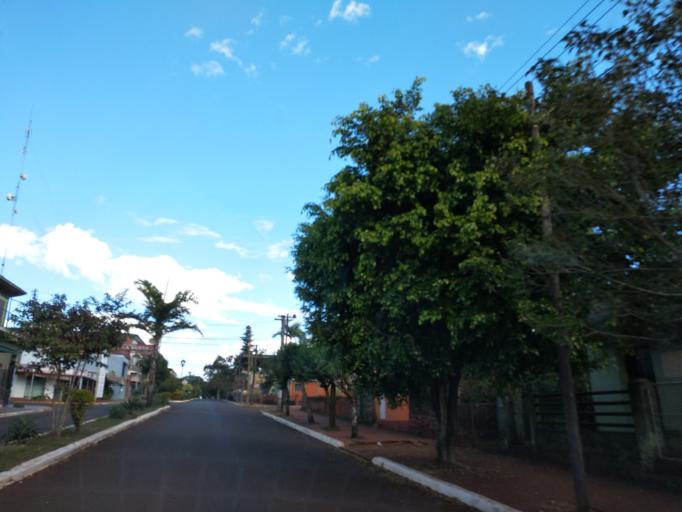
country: AR
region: Misiones
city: Jardin America
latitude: -27.0403
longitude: -55.2271
